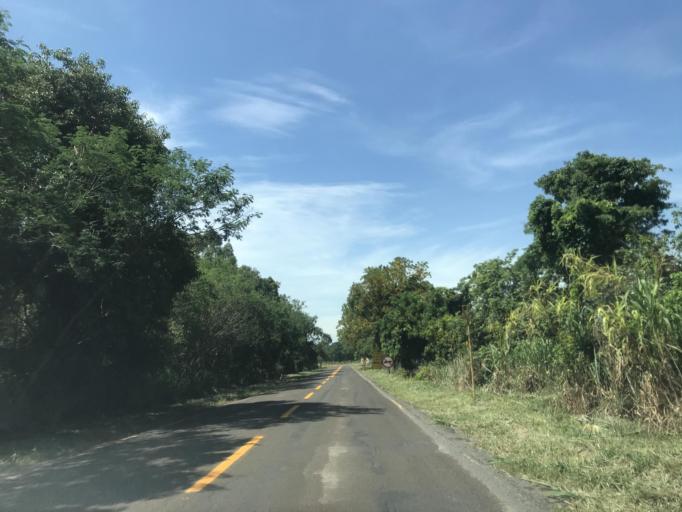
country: BR
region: Parana
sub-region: Terra Rica
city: Terra Rica
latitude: -22.7908
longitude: -52.6542
